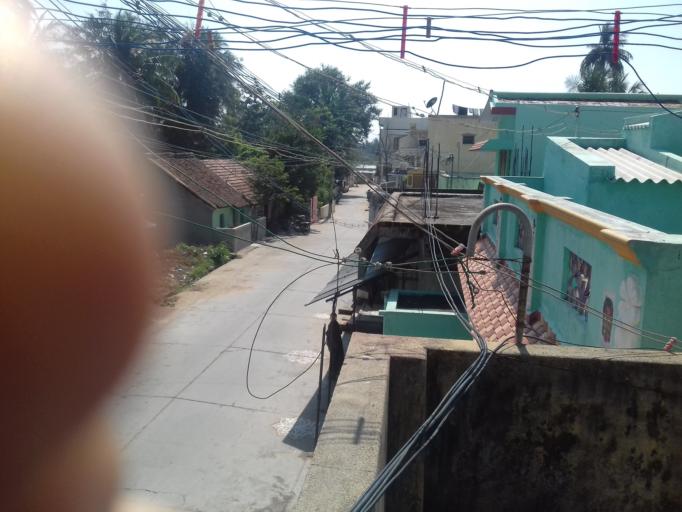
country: IN
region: Tamil Nadu
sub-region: Vellore
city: Arcot
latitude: 12.9822
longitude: 79.2665
